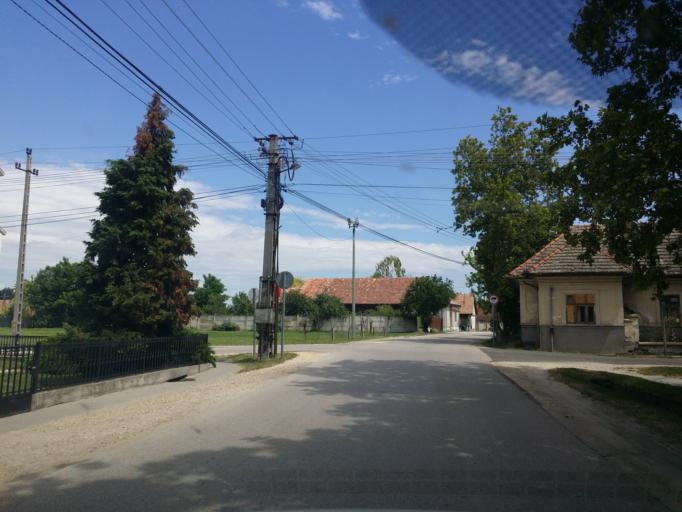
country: HU
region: Pest
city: Domsod
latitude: 47.0953
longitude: 19.0039
